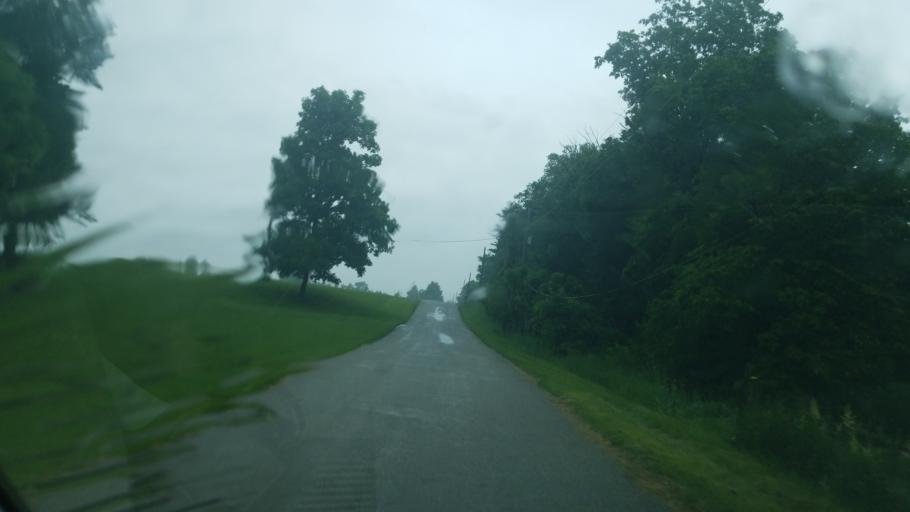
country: US
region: Ohio
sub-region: Richland County
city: Shelby
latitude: 40.9274
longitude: -82.7976
